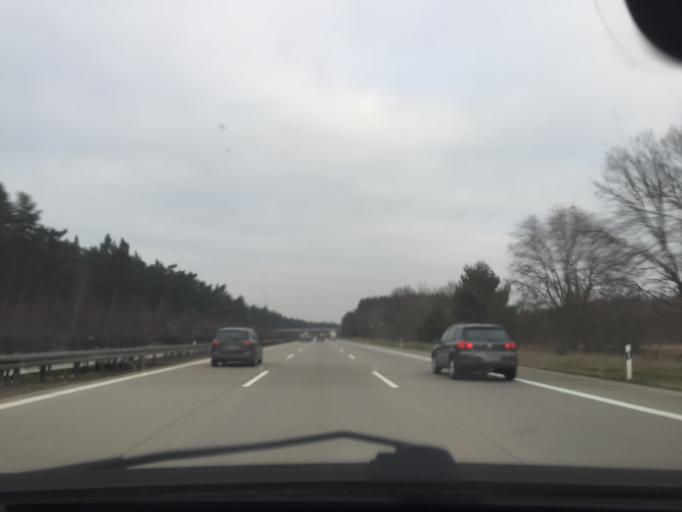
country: DE
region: Brandenburg
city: Wollin
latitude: 52.3310
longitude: 12.5020
